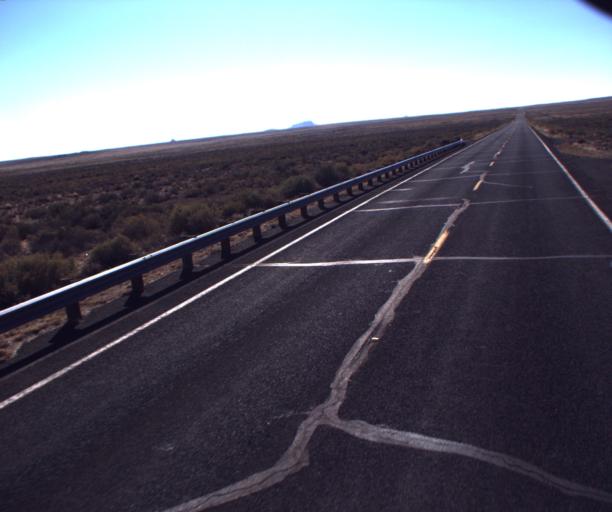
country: US
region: Arizona
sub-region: Navajo County
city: First Mesa
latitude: 35.6817
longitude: -110.5007
